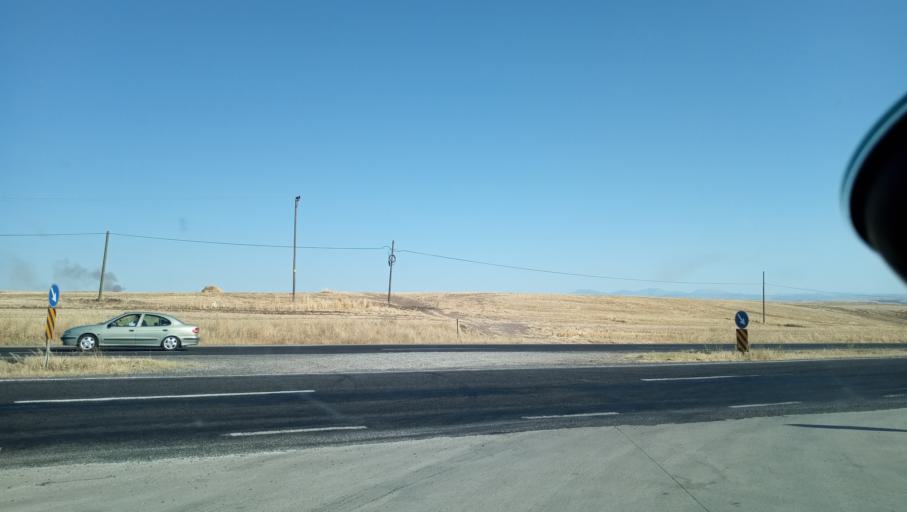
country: TR
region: Diyarbakir
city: Sur
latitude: 37.9786
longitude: 40.3604
